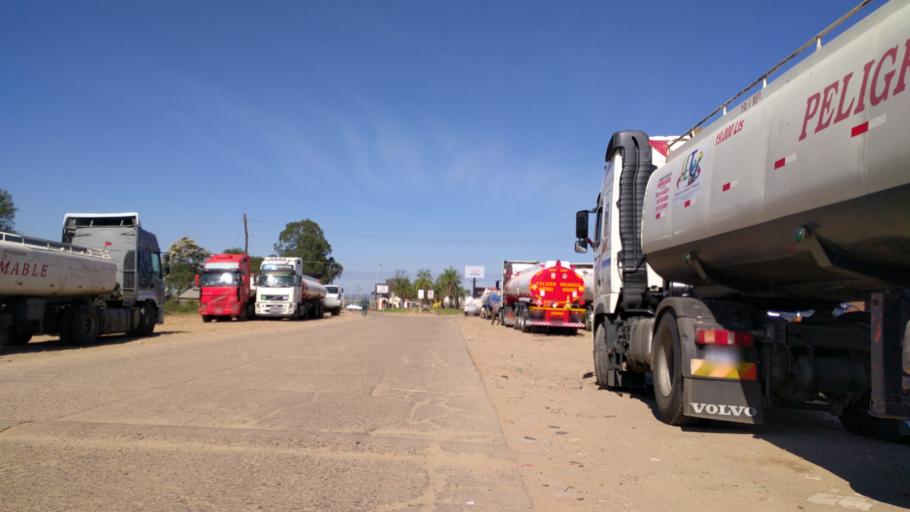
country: BO
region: Santa Cruz
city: Santa Cruz de la Sierra
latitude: -17.8740
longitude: -63.1931
